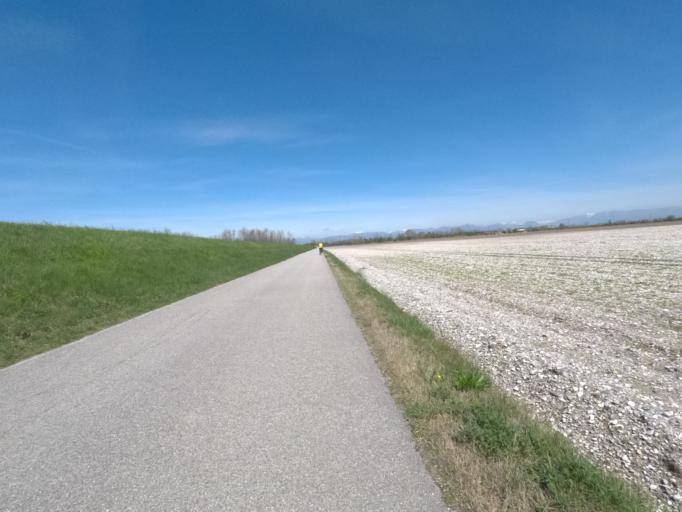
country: IT
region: Friuli Venezia Giulia
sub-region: Provincia di Udine
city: Camino al Tagliamento
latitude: 45.9532
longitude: 12.9144
